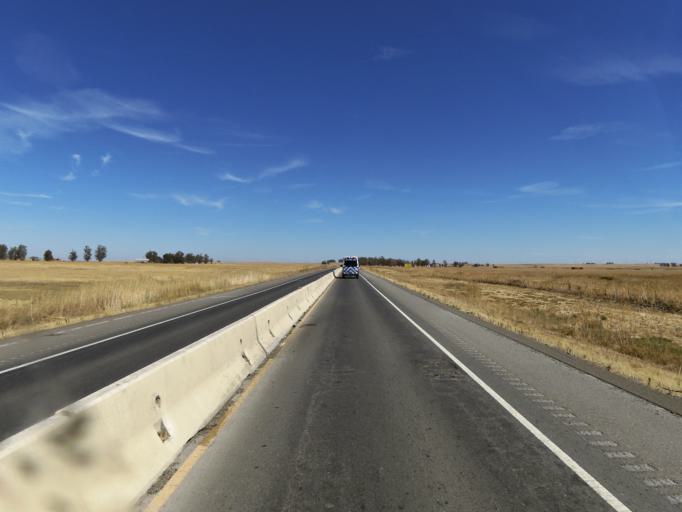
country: US
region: California
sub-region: Solano County
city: Suisun
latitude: 38.2283
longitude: -121.9182
